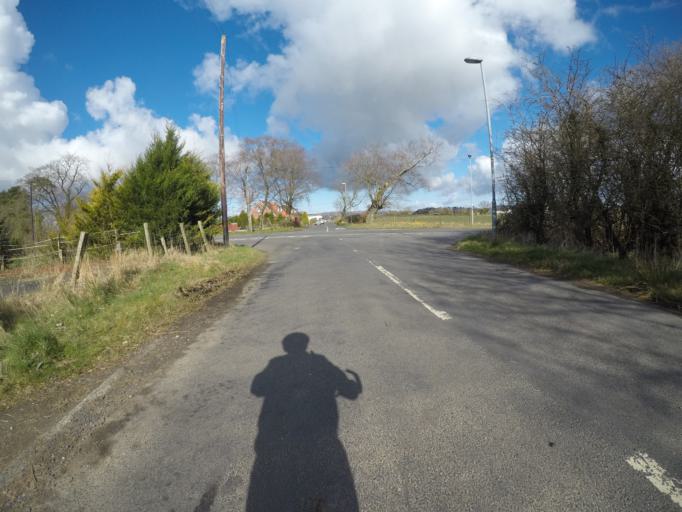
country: GB
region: Scotland
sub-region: North Ayrshire
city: Kilwinning
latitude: 55.6731
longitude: -4.6581
